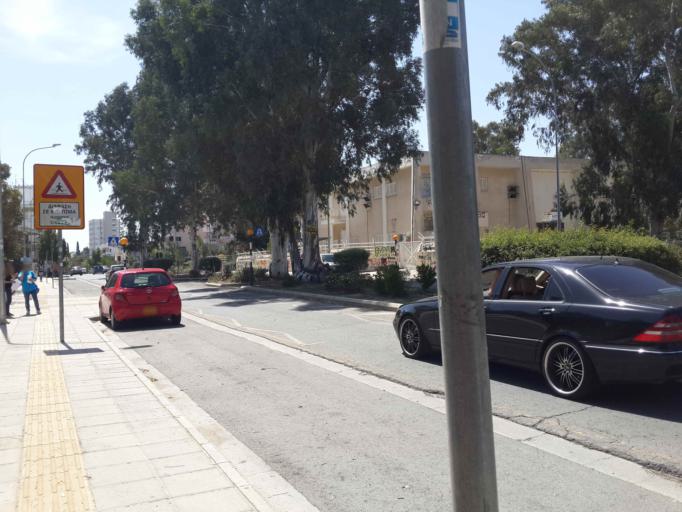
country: CY
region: Lefkosia
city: Nicosia
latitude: 35.1579
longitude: 33.3400
